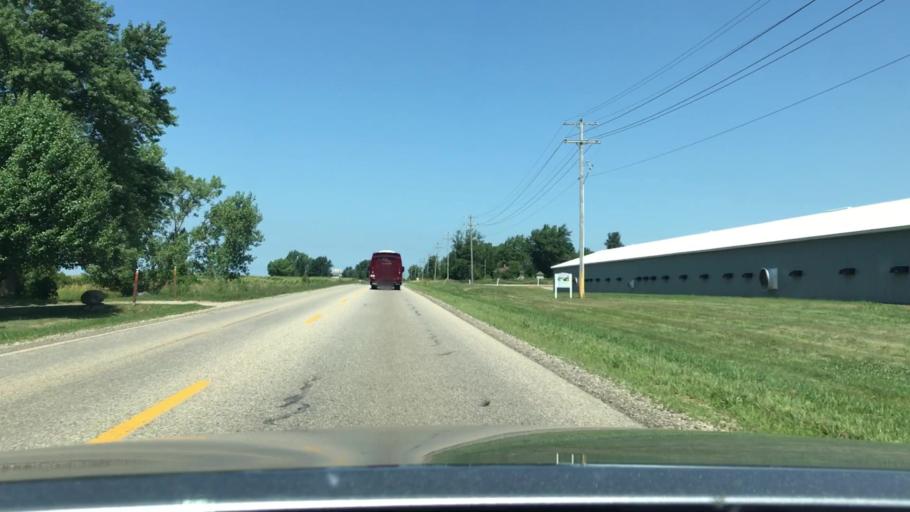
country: US
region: Michigan
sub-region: Ottawa County
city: Zeeland
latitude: 42.8605
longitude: -86.0795
